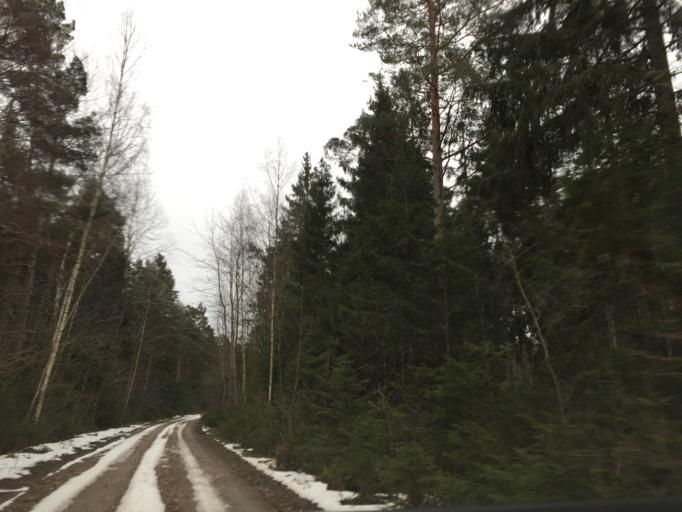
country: EE
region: Saare
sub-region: Kuressaare linn
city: Kuressaare
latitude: 58.4828
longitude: 22.2454
